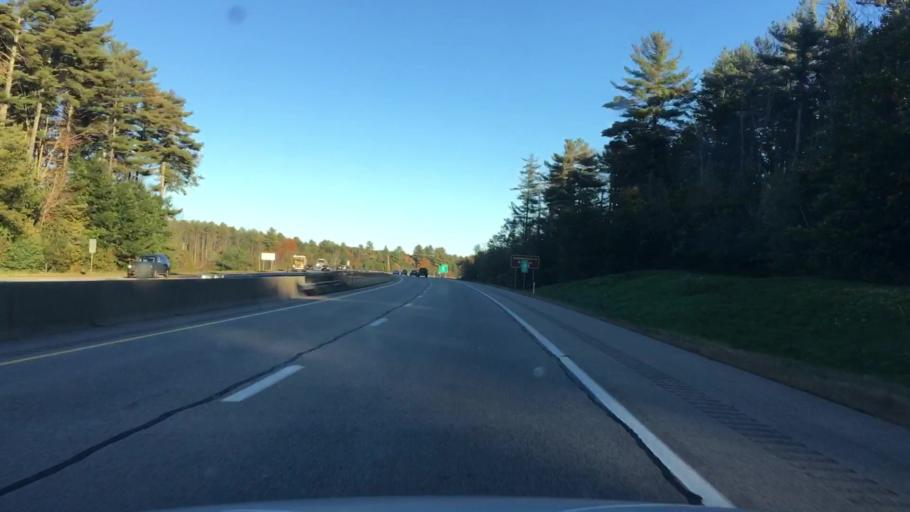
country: US
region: New Hampshire
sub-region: Rockingham County
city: Exeter
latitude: 43.0072
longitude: -70.9960
